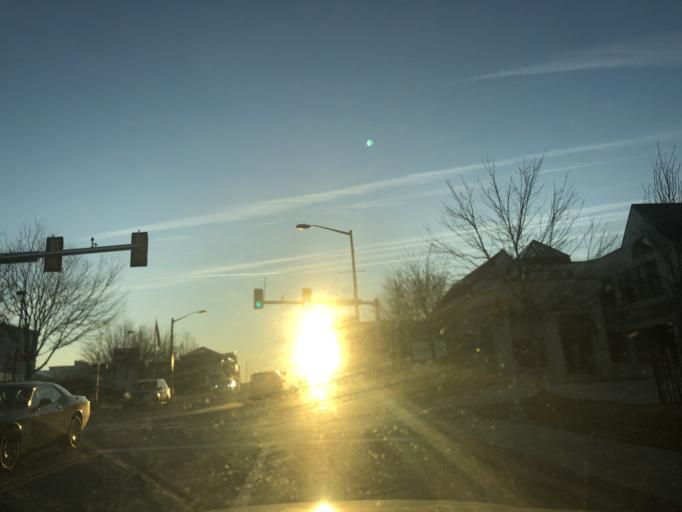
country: US
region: Pennsylvania
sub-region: Montgomery County
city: Bryn Mawr
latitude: 40.0200
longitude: -75.3152
